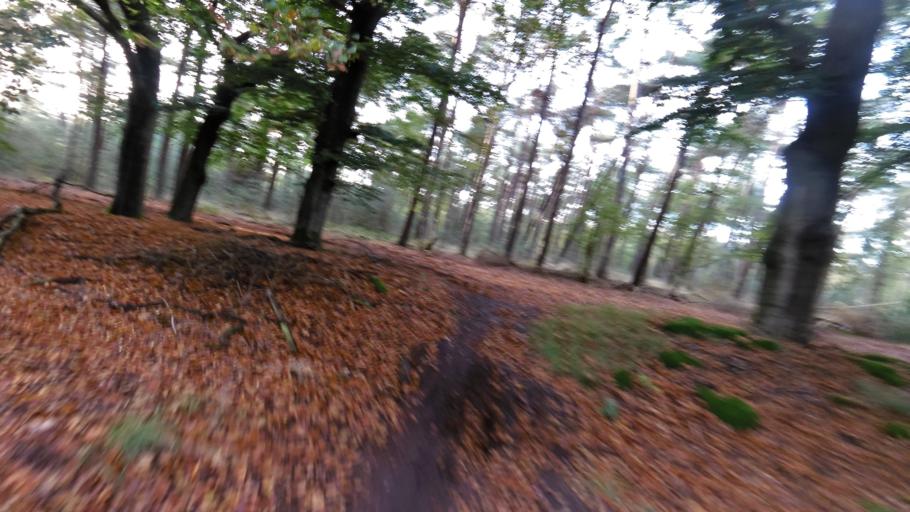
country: NL
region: Gelderland
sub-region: Gemeente Renkum
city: Wolfheze
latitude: 52.0272
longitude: 5.8165
